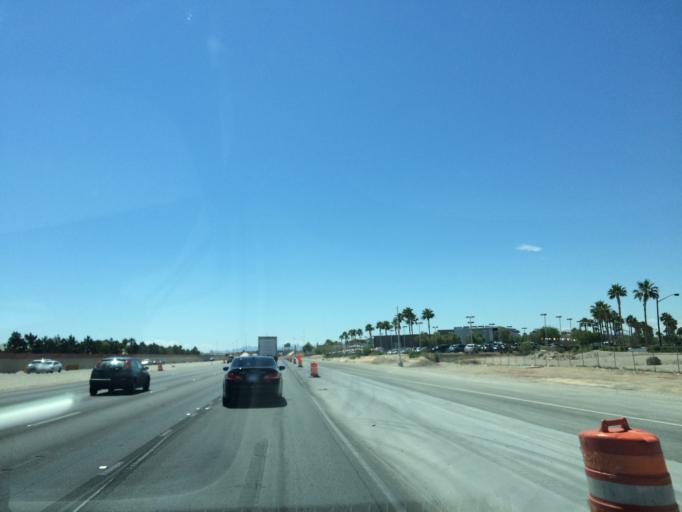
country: US
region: Nevada
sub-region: Clark County
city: Las Vegas
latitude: 36.2707
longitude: -115.2611
